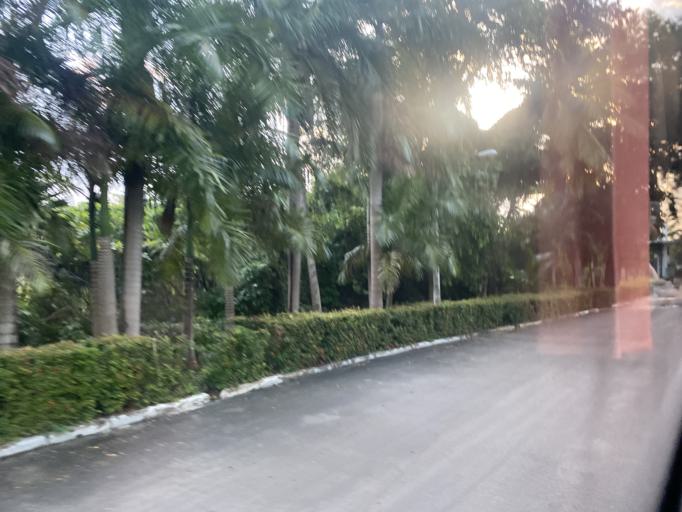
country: DO
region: San Juan
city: Punta Cana
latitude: 18.7151
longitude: -68.4586
